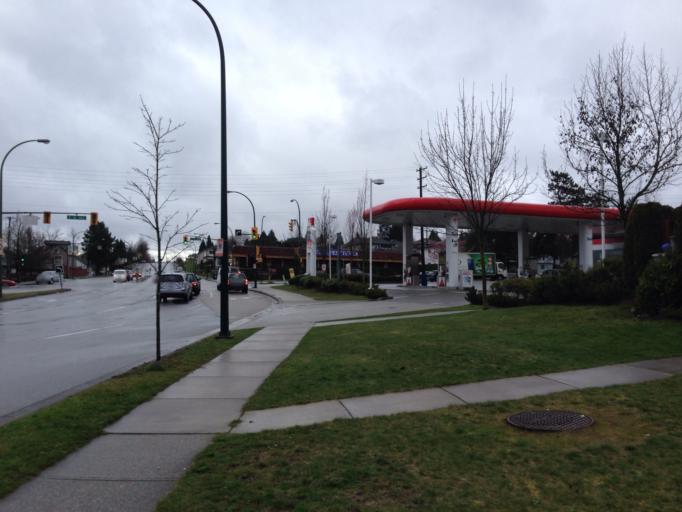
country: CA
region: British Columbia
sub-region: Fraser Valley Regional District
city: North Vancouver
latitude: 49.2702
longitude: -123.0338
